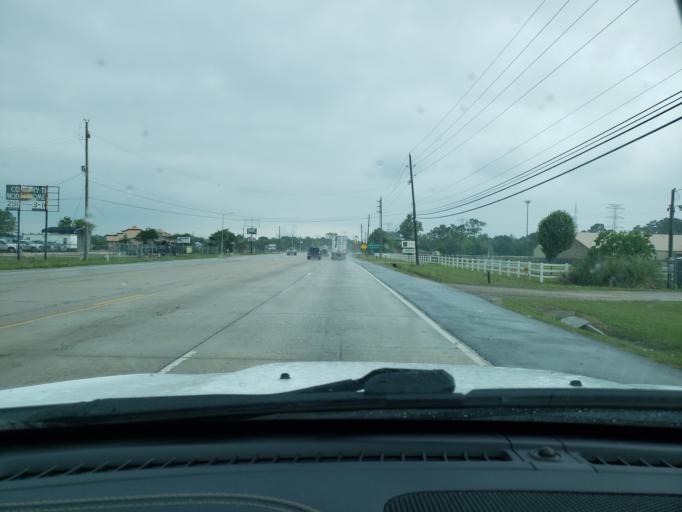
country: US
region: Texas
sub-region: Chambers County
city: Mont Belvieu
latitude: 29.8045
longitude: -94.9039
